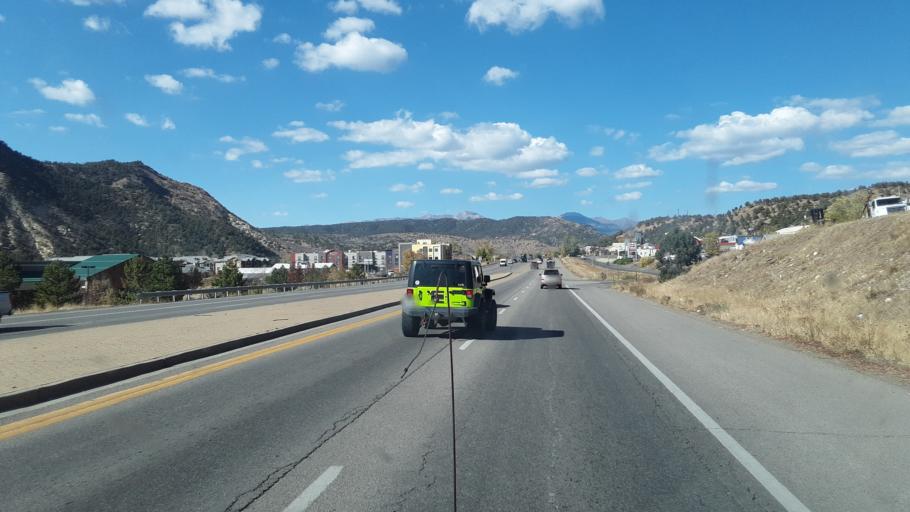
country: US
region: Colorado
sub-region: La Plata County
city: Durango
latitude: 37.2241
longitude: -107.8573
